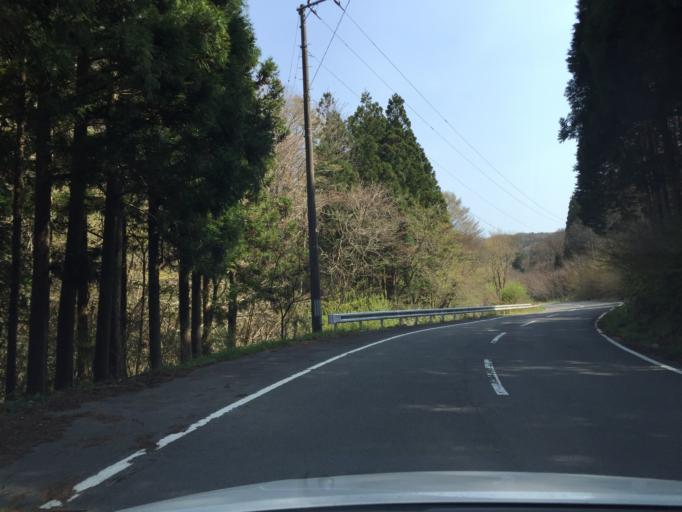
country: JP
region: Fukushima
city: Iwaki
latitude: 37.2347
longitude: 140.8451
